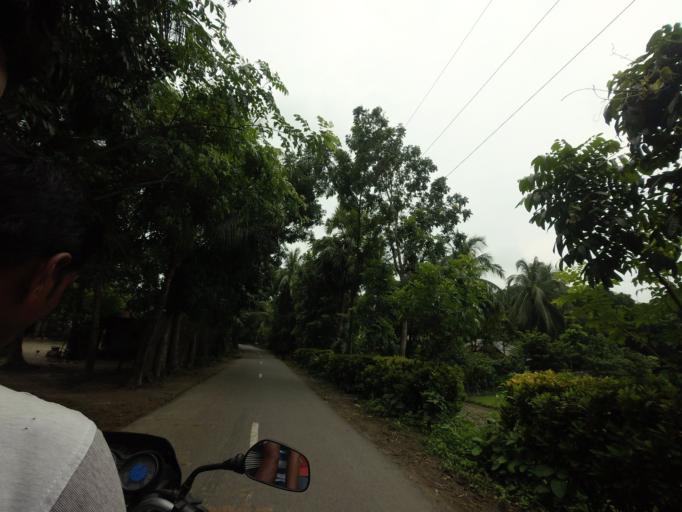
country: BD
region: Khulna
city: Kalia
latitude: 23.1121
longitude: 89.6469
